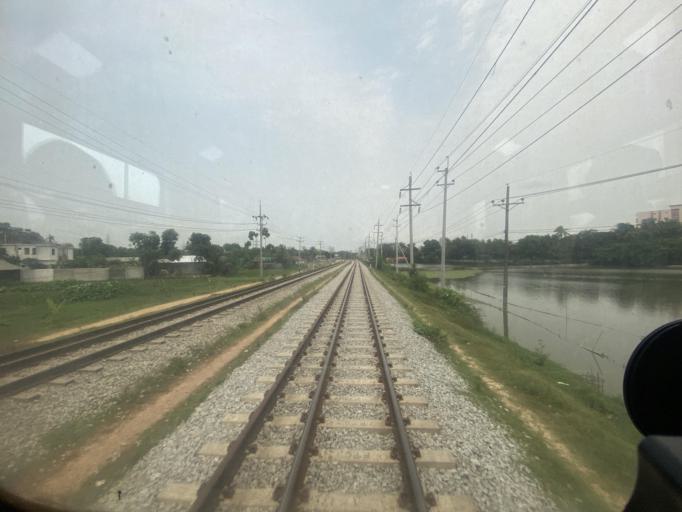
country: BD
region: Chittagong
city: Comilla
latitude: 23.4238
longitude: 91.1692
